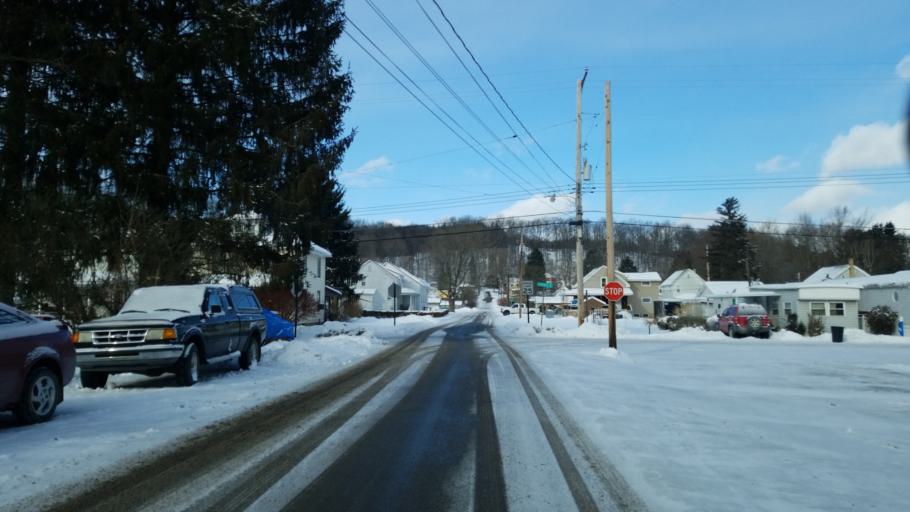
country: US
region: Pennsylvania
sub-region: Clearfield County
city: Hyde
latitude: 41.0015
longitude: -78.4644
